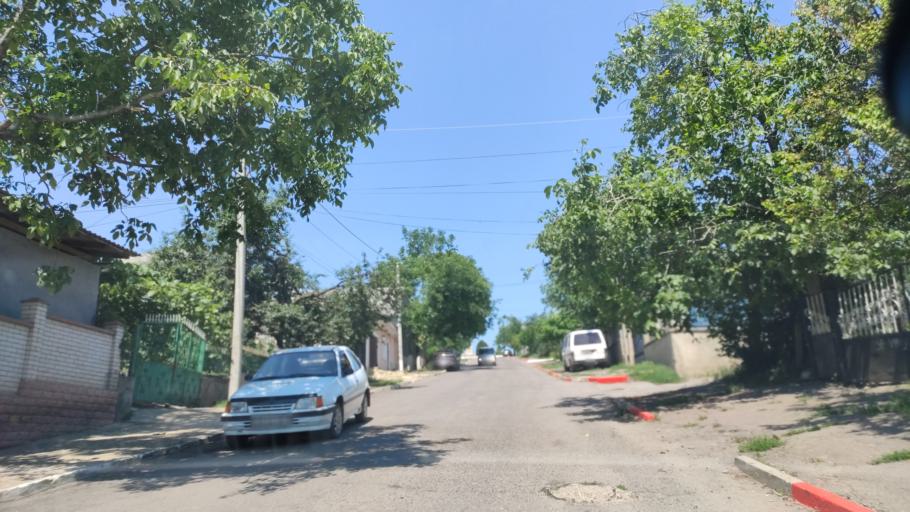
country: MD
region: Raionul Soroca
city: Soroca
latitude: 48.1718
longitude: 28.2968
